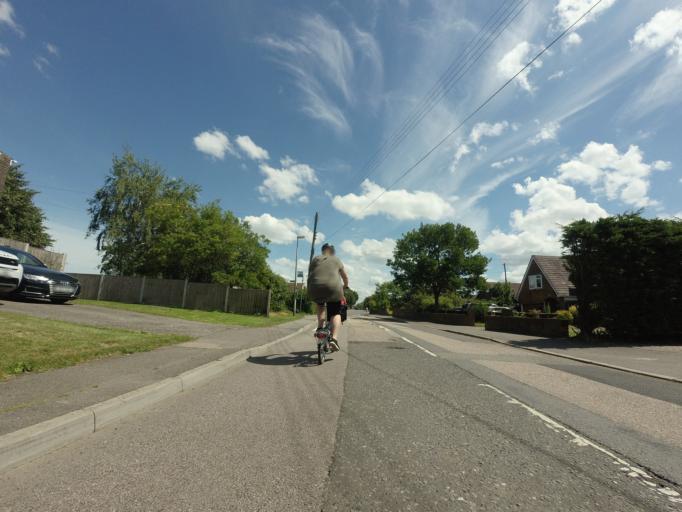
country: GB
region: England
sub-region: Medway
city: High Halstow
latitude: 51.4480
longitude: 0.5619
